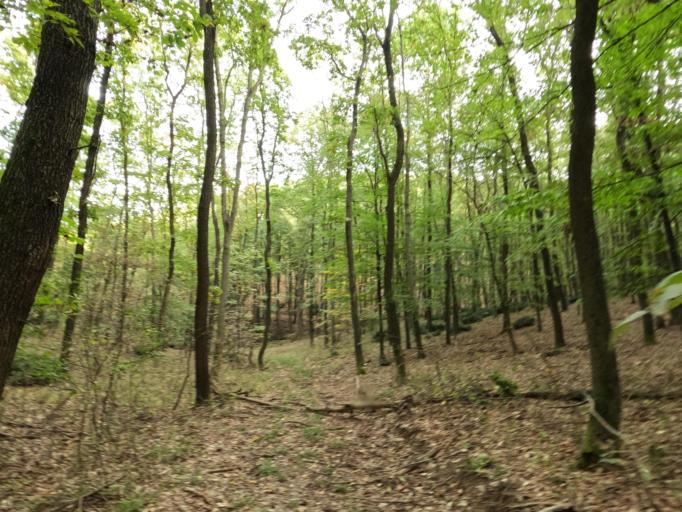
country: HU
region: Tolna
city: Szekszard
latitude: 46.3149
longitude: 18.6606
